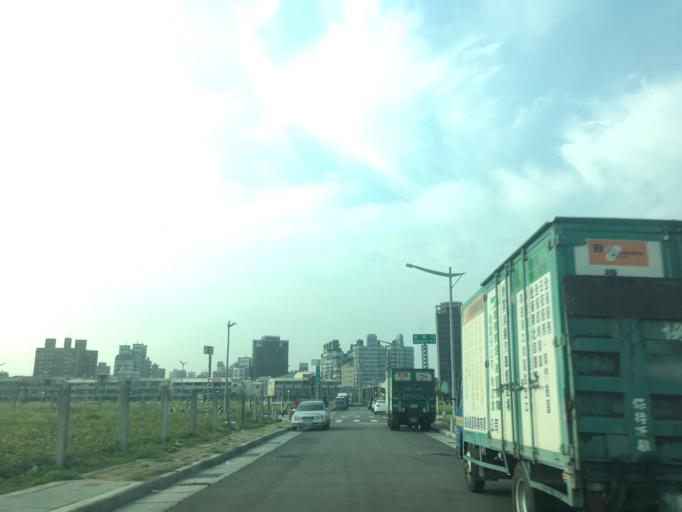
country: TW
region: Taiwan
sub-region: Taichung City
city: Taichung
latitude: 24.1867
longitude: 120.6917
